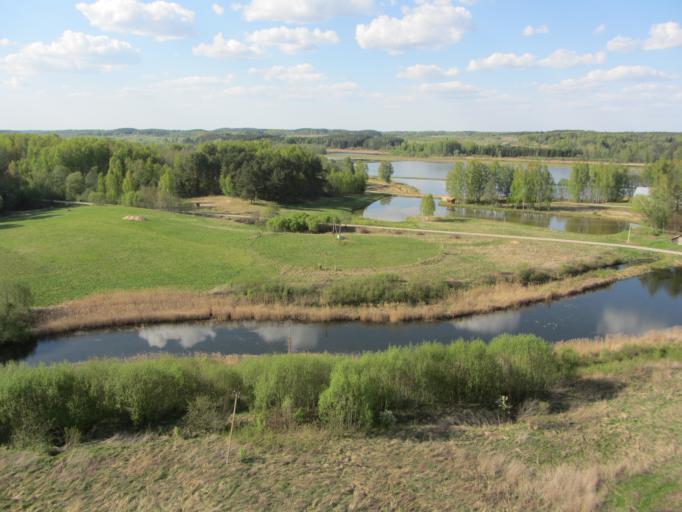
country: LT
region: Utenos apskritis
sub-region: Utena
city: Utena
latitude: 55.6944
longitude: 25.8002
